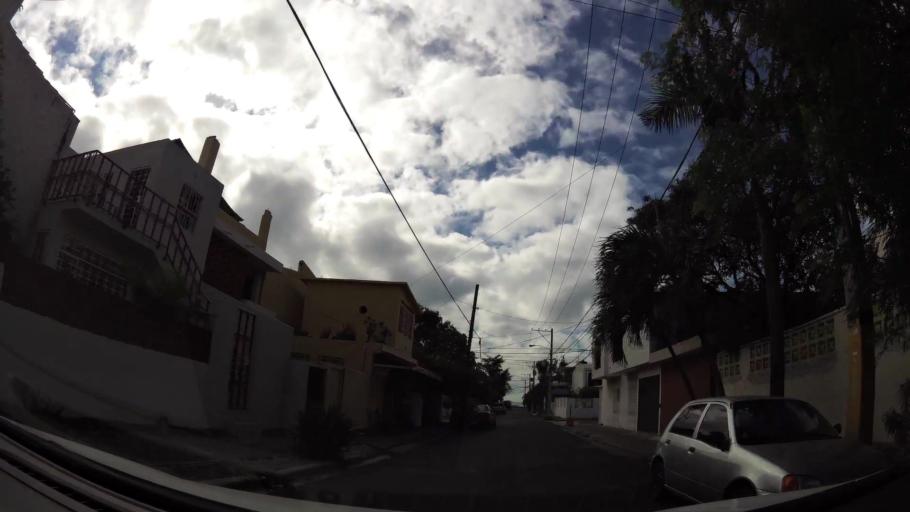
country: DO
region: Nacional
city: Bella Vista
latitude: 18.4442
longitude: -69.9289
